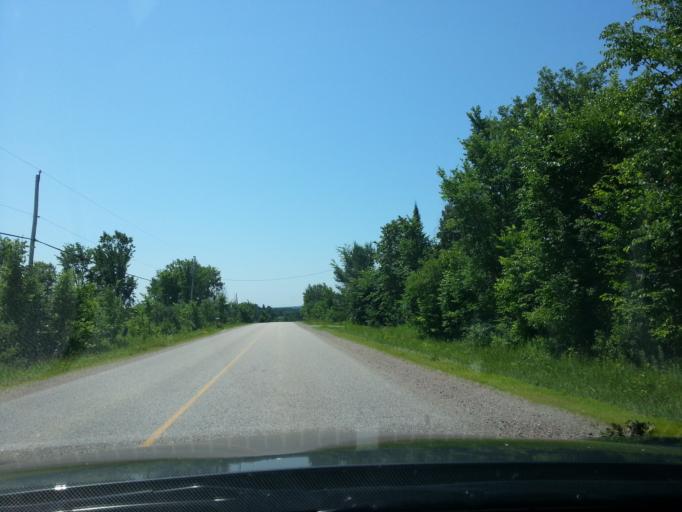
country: CA
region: Ontario
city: Arnprior
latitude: 45.5373
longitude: -76.3690
